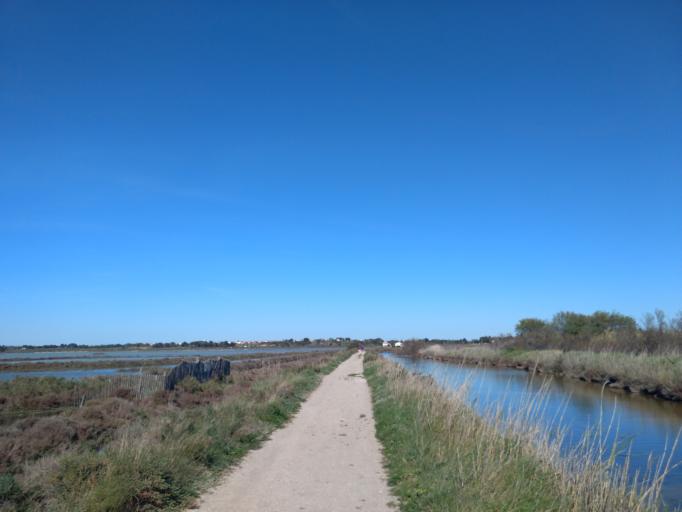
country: FR
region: Languedoc-Roussillon
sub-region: Departement de l'Herault
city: Villeneuve-les-Maguelone
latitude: 43.5119
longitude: 3.8408
